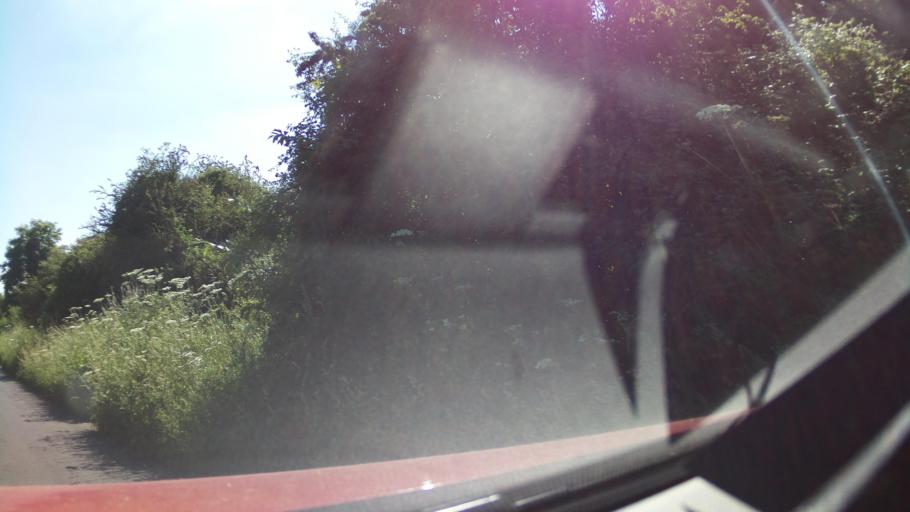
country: GB
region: England
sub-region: Hampshire
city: Abbotts Ann
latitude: 51.2214
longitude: -1.5670
